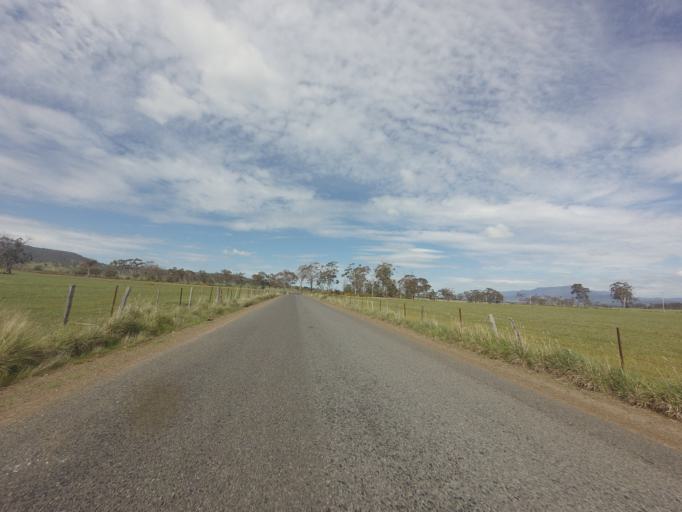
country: AU
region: Tasmania
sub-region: Northern Midlands
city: Longford
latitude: -41.7361
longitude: 147.1996
